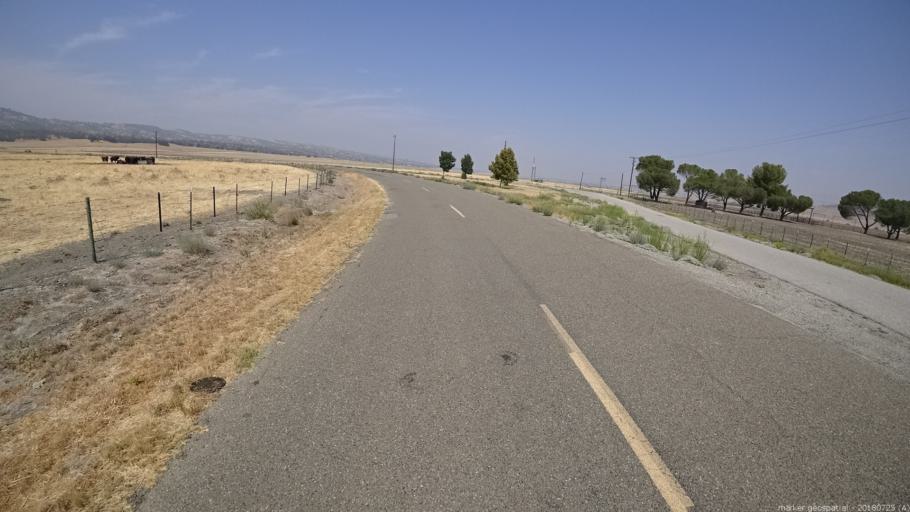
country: US
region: California
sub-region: San Luis Obispo County
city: Shandon
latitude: 35.8051
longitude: -120.3549
